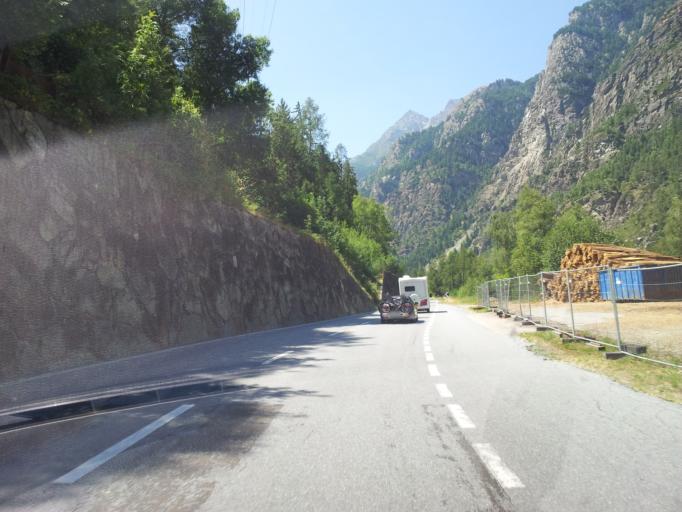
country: CH
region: Valais
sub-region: Visp District
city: Grachen
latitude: 46.2060
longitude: 7.8308
